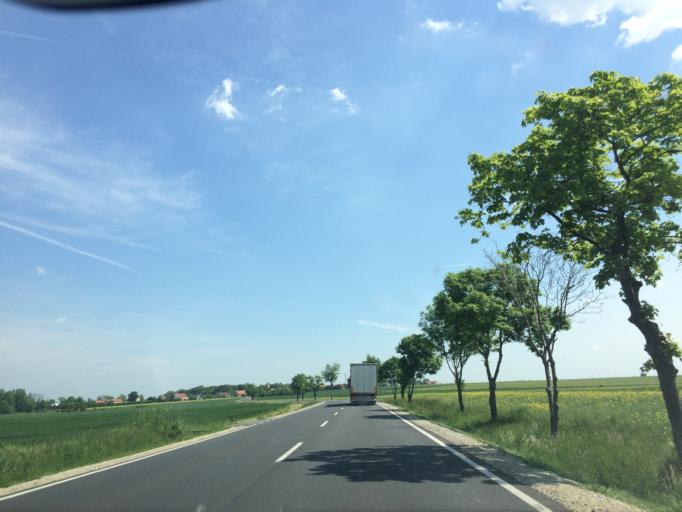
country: PL
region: Lower Silesian Voivodeship
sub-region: Powiat wroclawski
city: Sobotka
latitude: 50.9396
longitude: 16.7165
